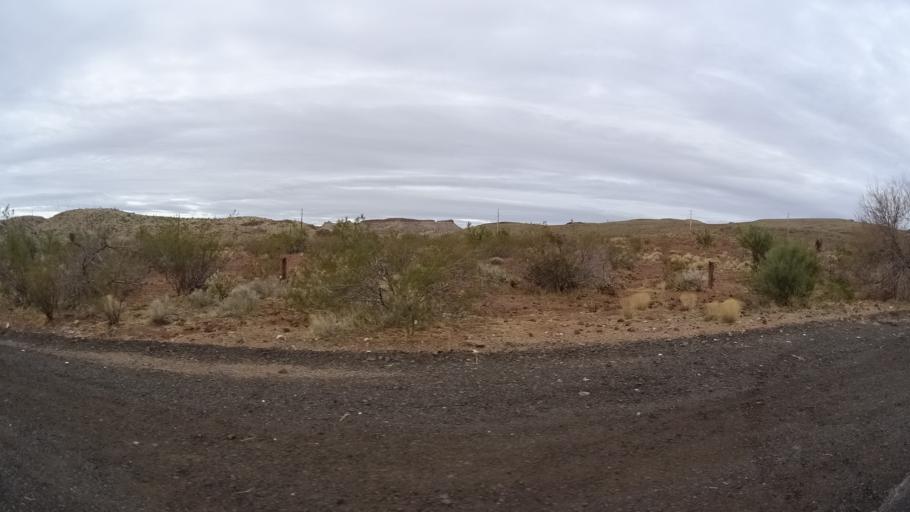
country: US
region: Arizona
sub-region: Mohave County
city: Kingman
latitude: 35.2062
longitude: -114.0809
